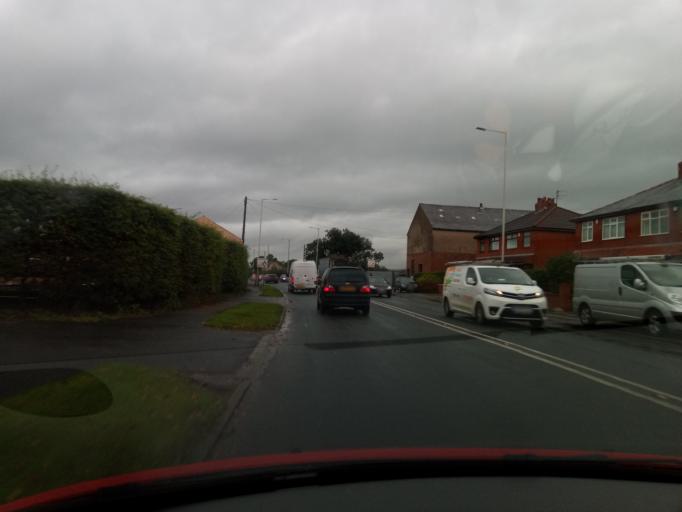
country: GB
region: England
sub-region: Lancashire
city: Catterall
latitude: 53.8602
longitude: -2.7438
